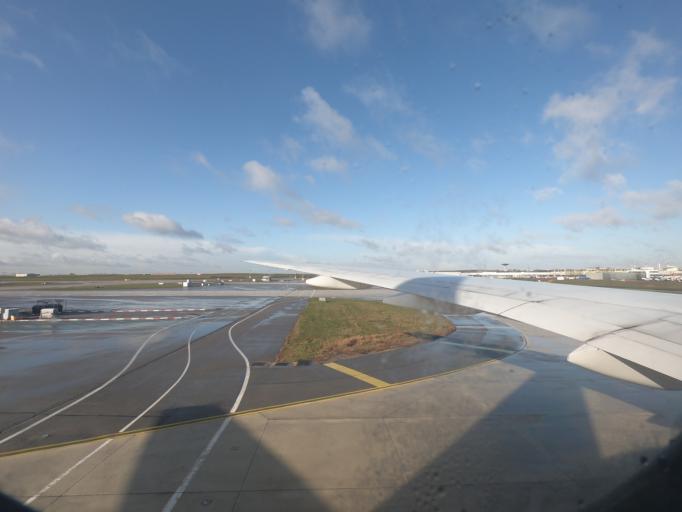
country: FR
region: Ile-de-France
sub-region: Departement du Val-d'Oise
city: Roissy-en-France
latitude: 48.9986
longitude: 2.5542
